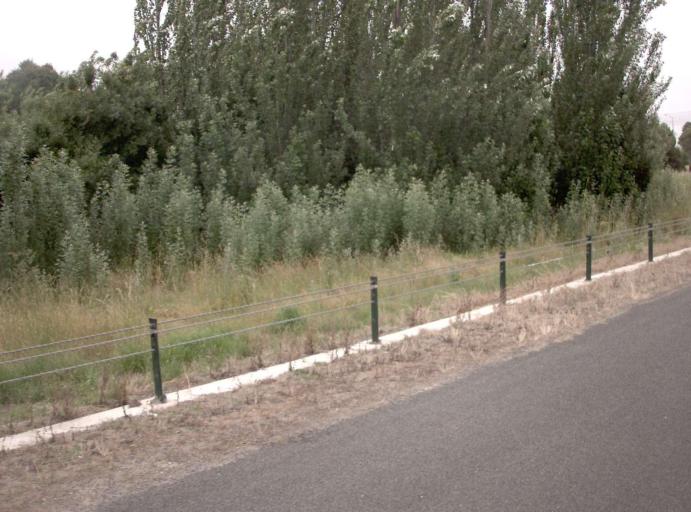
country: AU
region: Victoria
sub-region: Latrobe
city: Morwell
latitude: -38.2448
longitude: 146.4387
